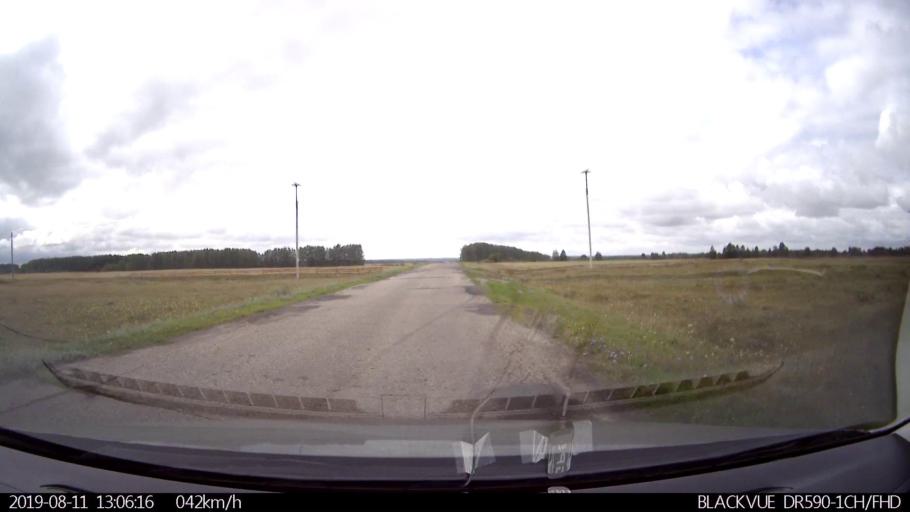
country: RU
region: Ulyanovsk
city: Ignatovka
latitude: 53.8679
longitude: 47.6458
